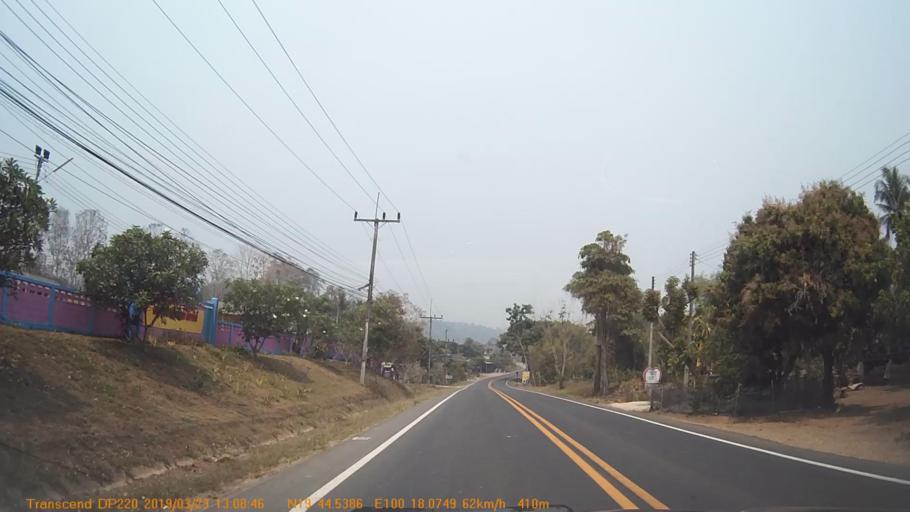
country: TH
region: Chiang Rai
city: Khun Tan
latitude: 19.7424
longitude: 100.3013
